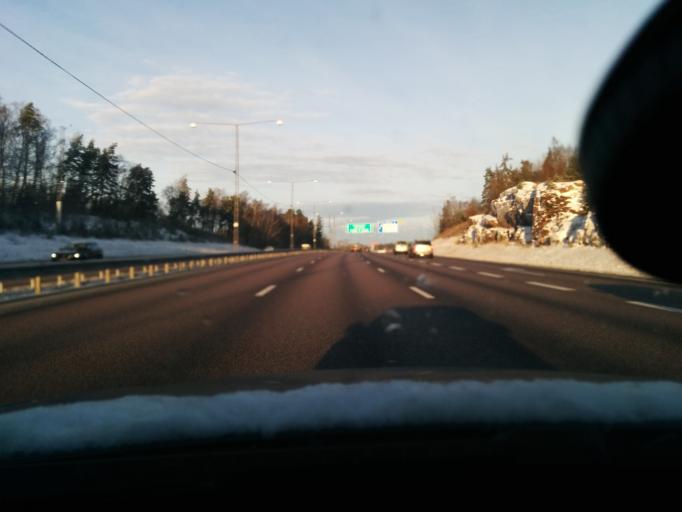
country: SE
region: Stockholm
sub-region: Upplands Vasby Kommun
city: Upplands Vaesby
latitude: 59.4894
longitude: 17.9197
